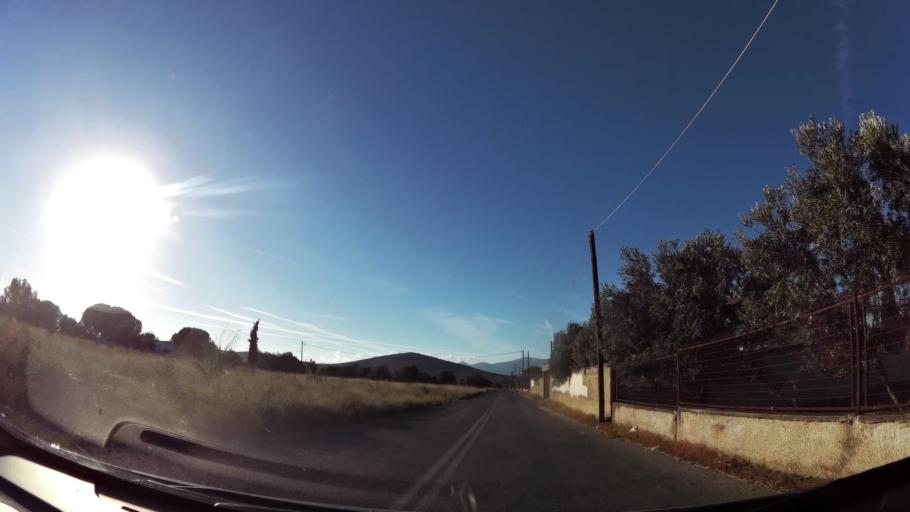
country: GR
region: Attica
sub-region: Nomarchia Anatolikis Attikis
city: Kalyvia Thorikou
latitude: 37.8454
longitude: 23.9214
